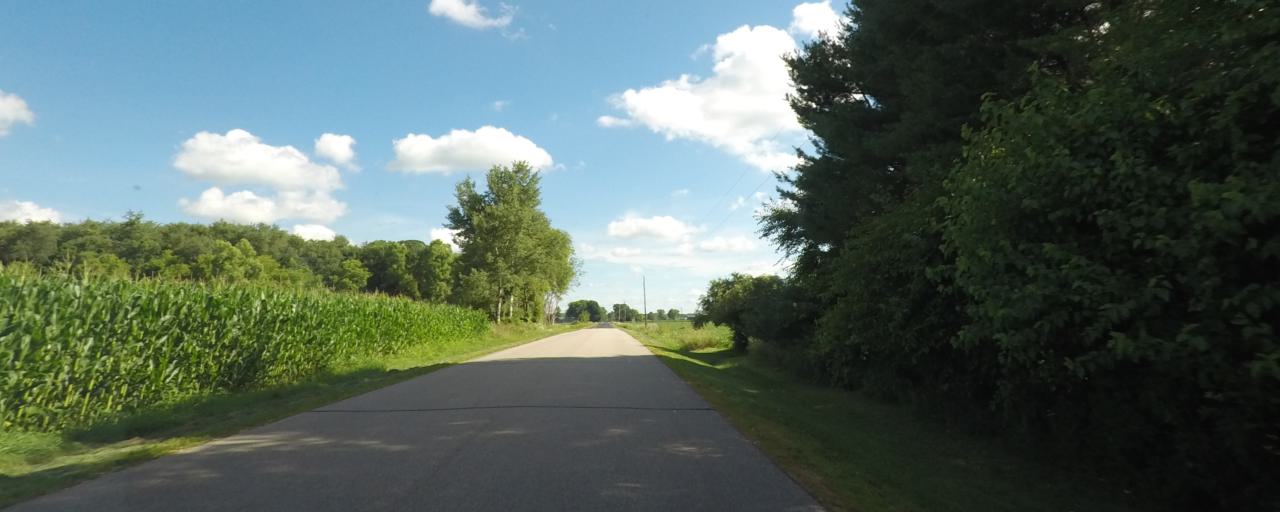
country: US
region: Wisconsin
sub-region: Rock County
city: Edgerton
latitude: 42.8920
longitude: -89.1321
